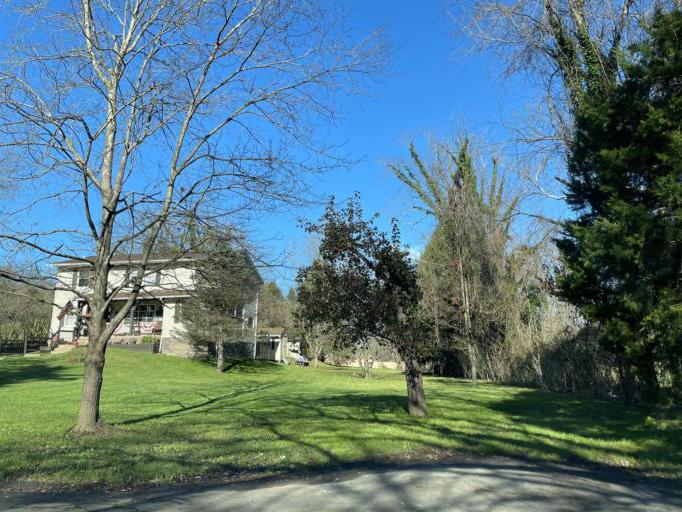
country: US
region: Maryland
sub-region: Baltimore County
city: Mays Chapel
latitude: 39.4071
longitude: -76.6489
